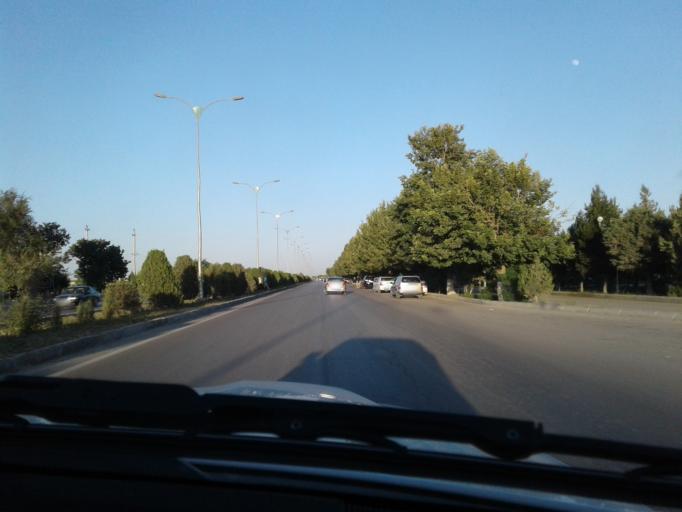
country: TM
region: Ahal
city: Abadan
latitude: 38.1637
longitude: 57.9422
